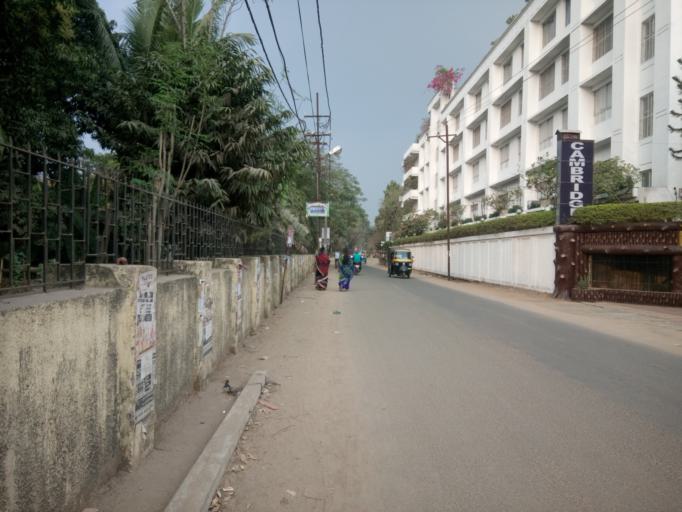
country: IN
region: Odisha
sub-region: Cuttack
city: Cuttack
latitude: 20.4808
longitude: 85.8613
